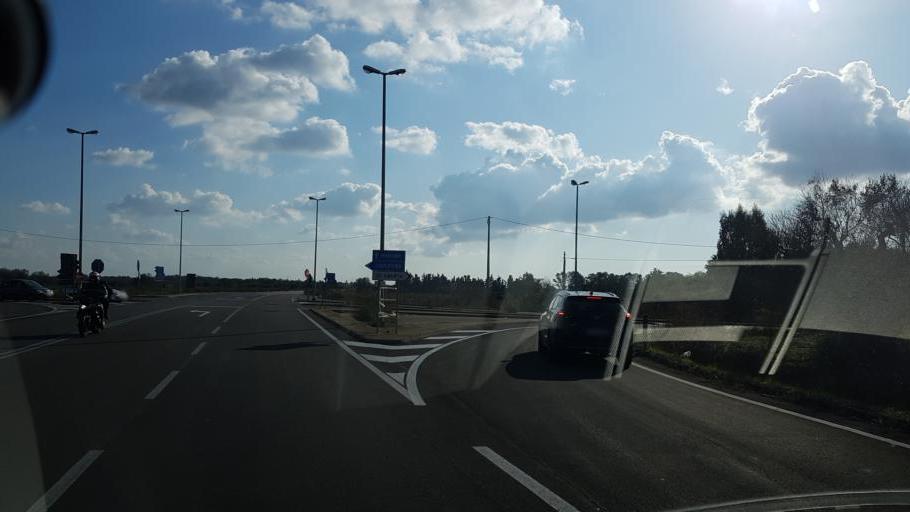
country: IT
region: Apulia
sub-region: Provincia di Lecce
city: Veglie
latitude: 40.3366
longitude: 17.9814
